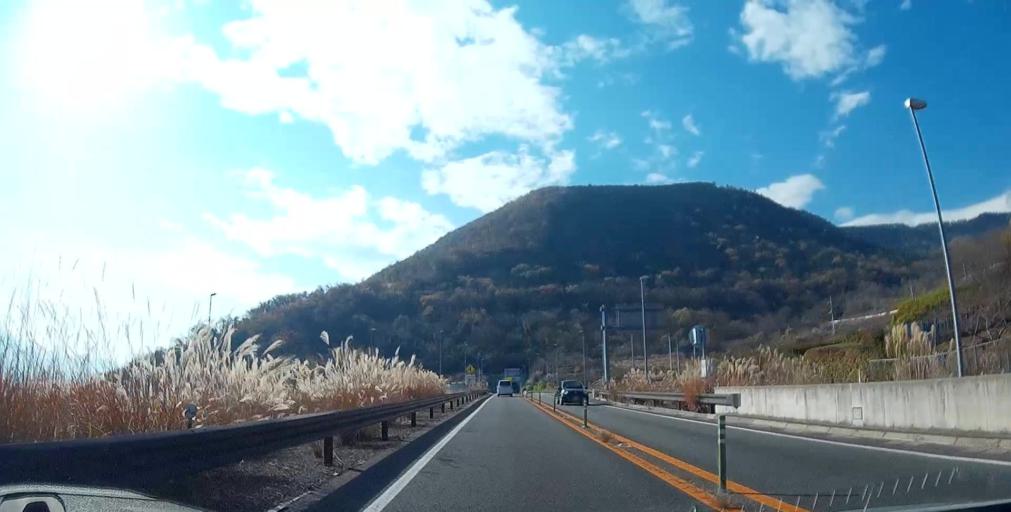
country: JP
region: Yamanashi
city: Isawa
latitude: 35.6693
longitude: 138.6410
